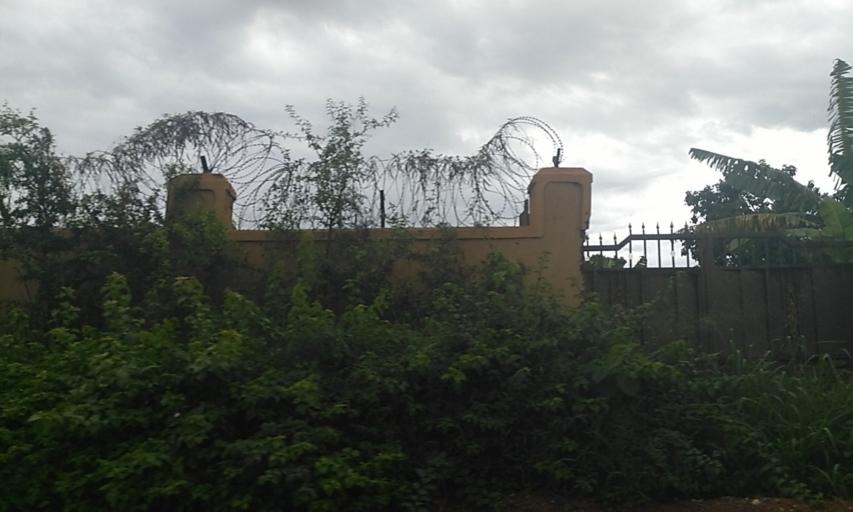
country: UG
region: Central Region
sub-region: Wakiso District
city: Bweyogerere
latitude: 0.3606
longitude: 32.6659
